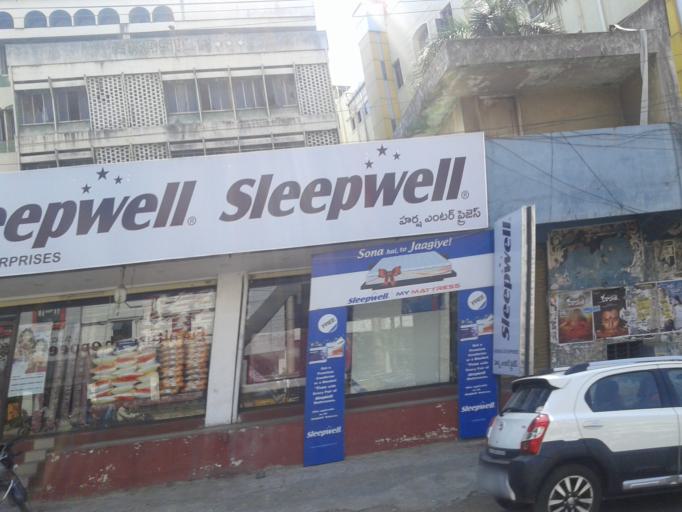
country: IN
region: Telangana
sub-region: Warangal
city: Warangal
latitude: 17.9979
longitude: 79.5874
